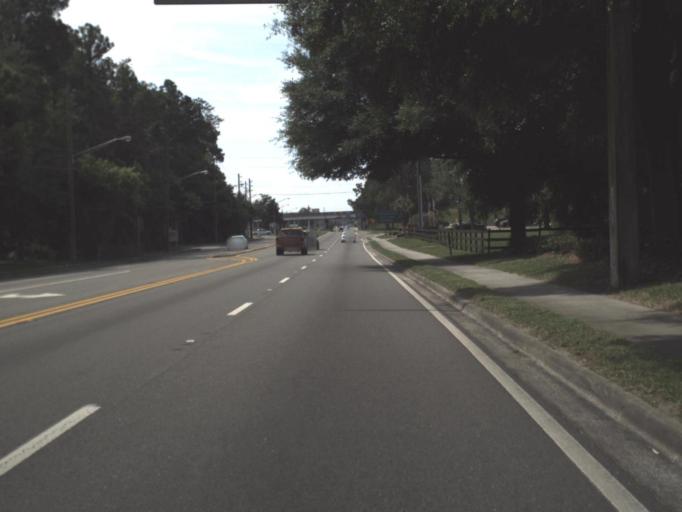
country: US
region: Florida
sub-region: Duval County
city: Jacksonville
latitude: 30.3002
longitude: -81.6014
